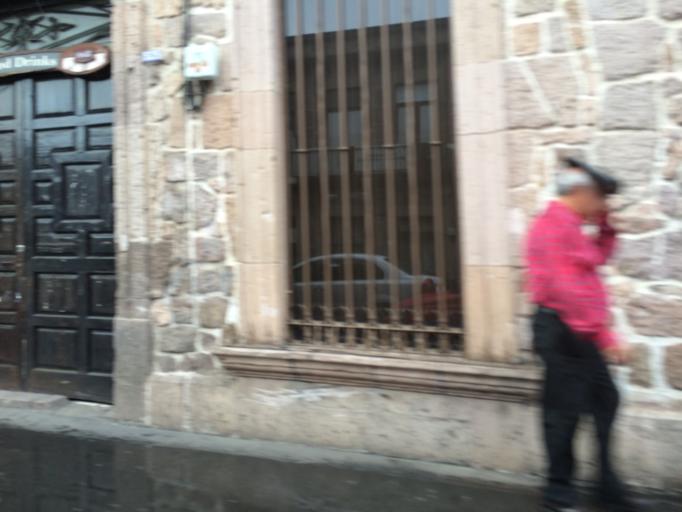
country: MX
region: Michoacan
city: Morelia
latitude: 19.7031
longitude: -101.1962
